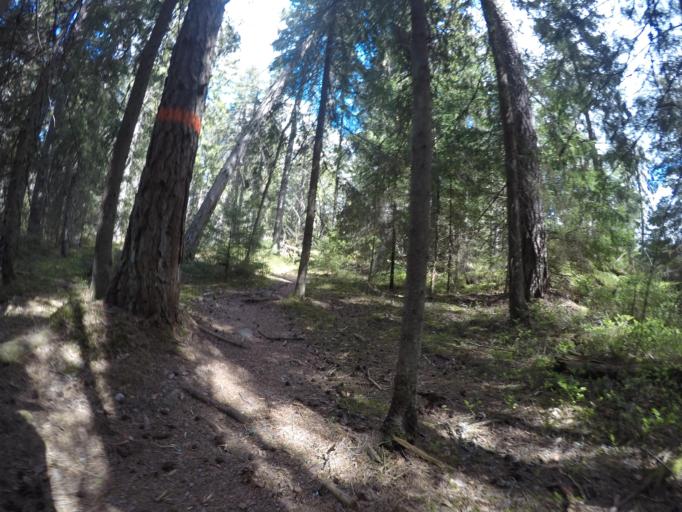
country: SE
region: Soedermanland
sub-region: Eskilstuna Kommun
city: Hallbybrunn
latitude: 59.3521
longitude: 16.4002
